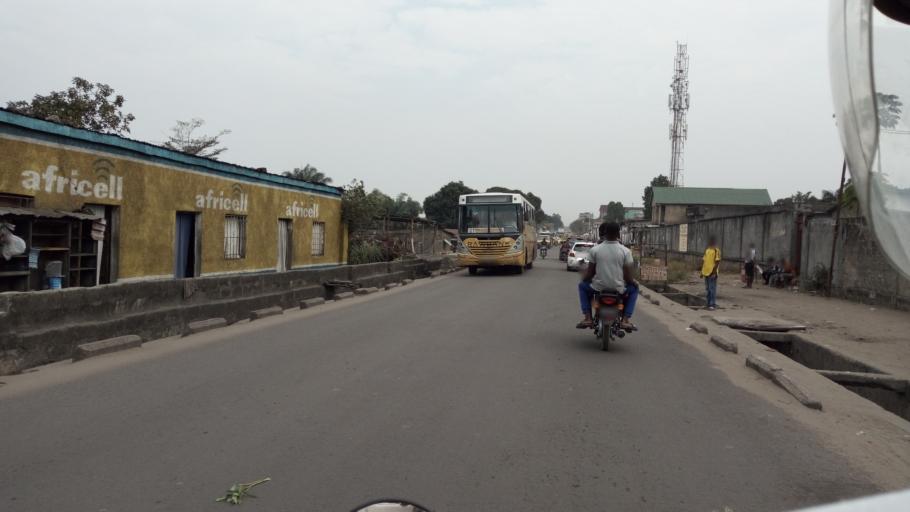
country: CD
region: Kinshasa
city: Masina
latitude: -4.4084
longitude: 15.3163
